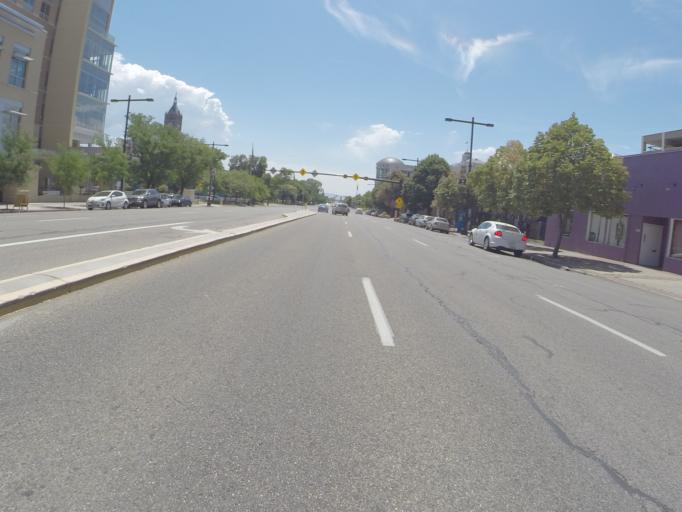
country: US
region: Utah
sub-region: Salt Lake County
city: Salt Lake City
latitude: 40.7621
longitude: -111.8883
